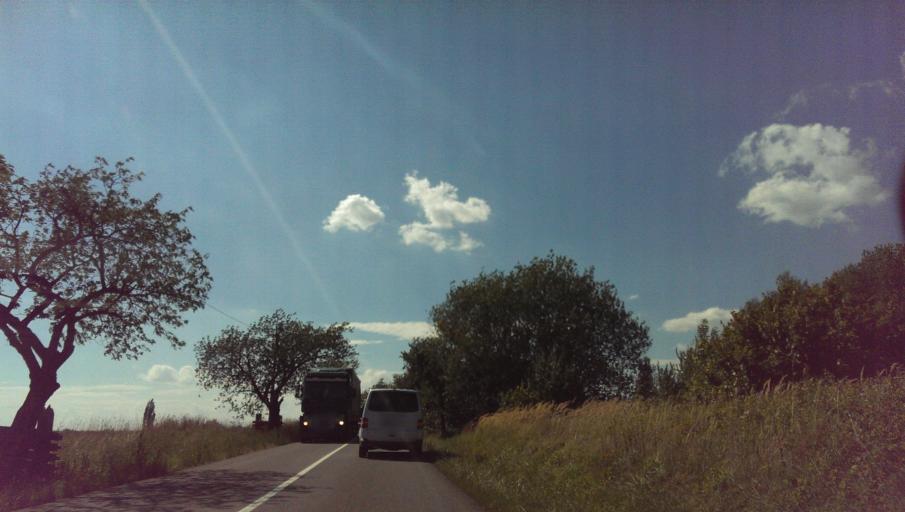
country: CZ
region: Zlin
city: Kelc
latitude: 49.4423
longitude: 17.8276
